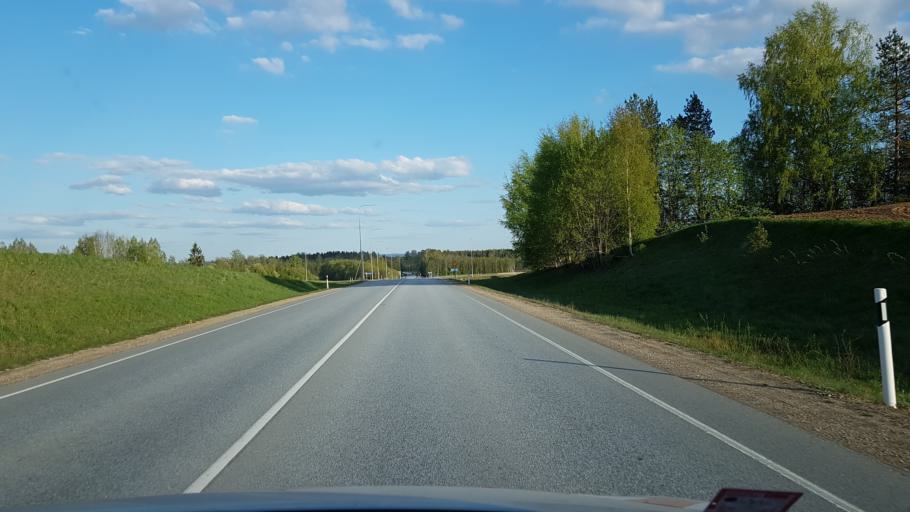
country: EE
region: Vorumaa
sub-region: Voru linn
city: Voru
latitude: 57.8934
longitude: 26.8470
